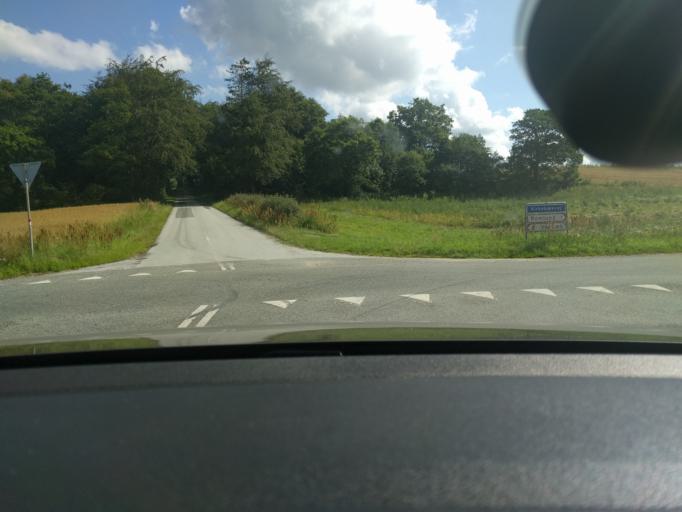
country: DK
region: Central Jutland
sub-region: Viborg Kommune
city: Viborg
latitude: 56.4938
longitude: 9.2873
